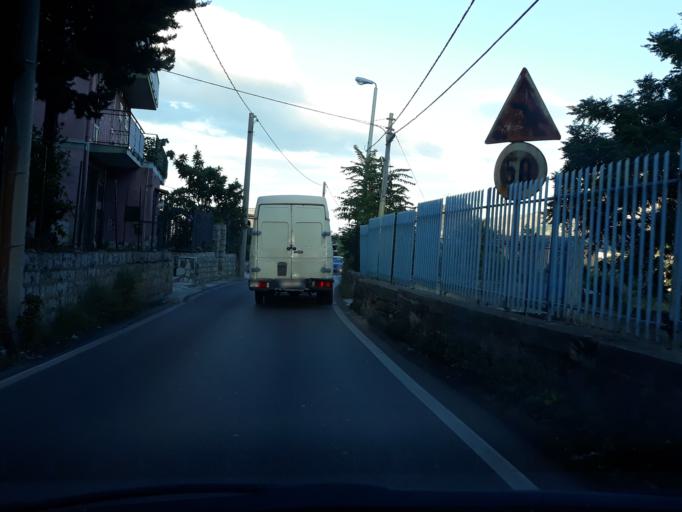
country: IT
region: Sicily
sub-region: Palermo
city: Villa Ciambra
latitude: 38.0786
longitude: 13.3144
